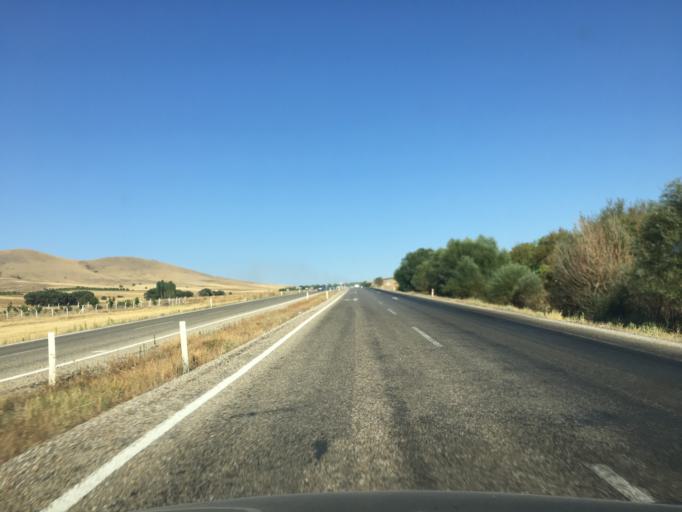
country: TR
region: Kirsehir
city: Kaman
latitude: 39.3722
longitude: 33.8534
